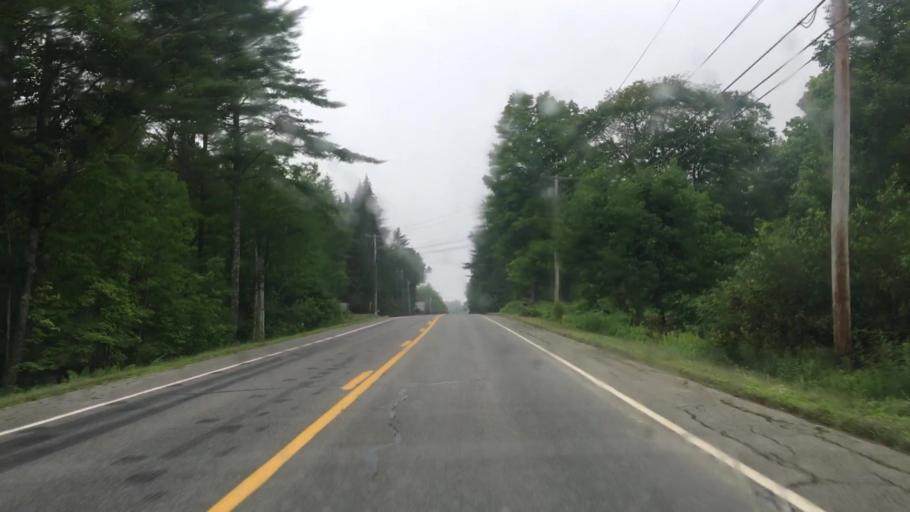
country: US
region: Maine
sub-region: Lincoln County
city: Wiscasset
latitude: 44.0572
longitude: -69.6854
